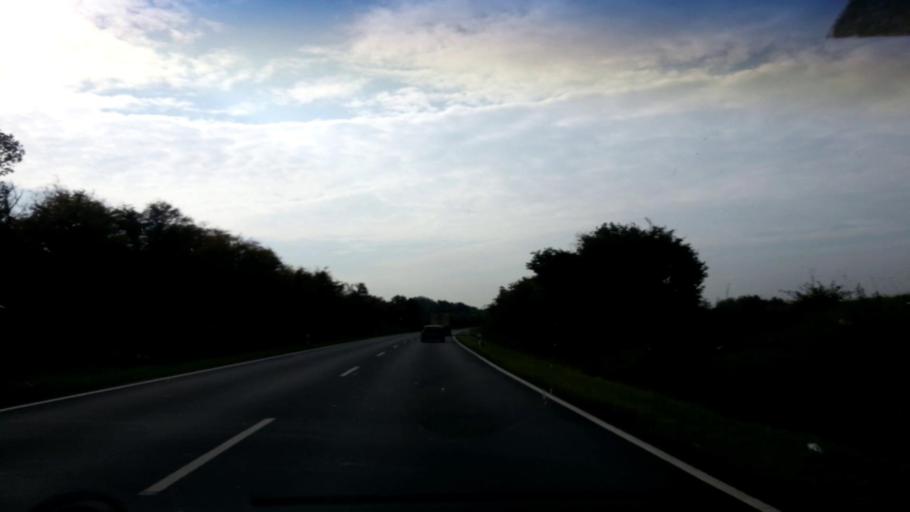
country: DE
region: Bavaria
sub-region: Regierungsbezirk Unterfranken
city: Prichsenstadt
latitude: 49.8388
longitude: 10.3531
